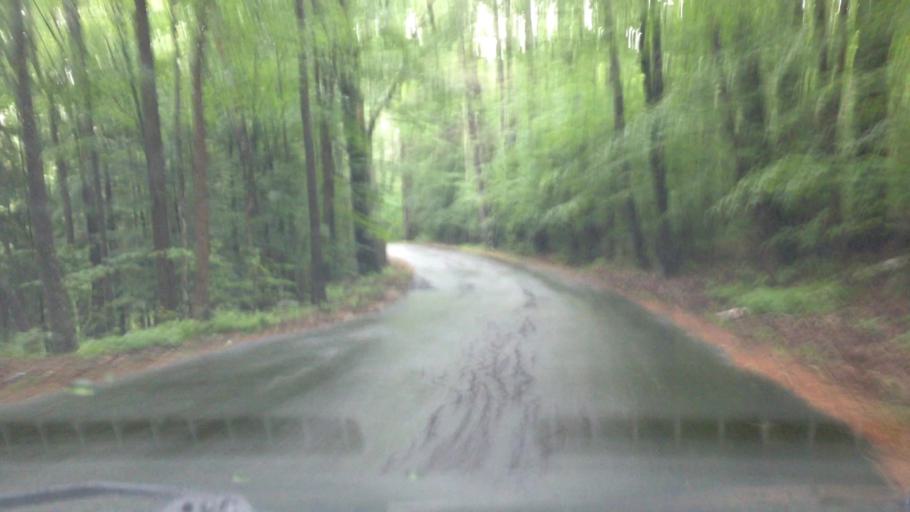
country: US
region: New Hampshire
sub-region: Cheshire County
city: Marlborough
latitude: 42.8956
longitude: -72.1959
